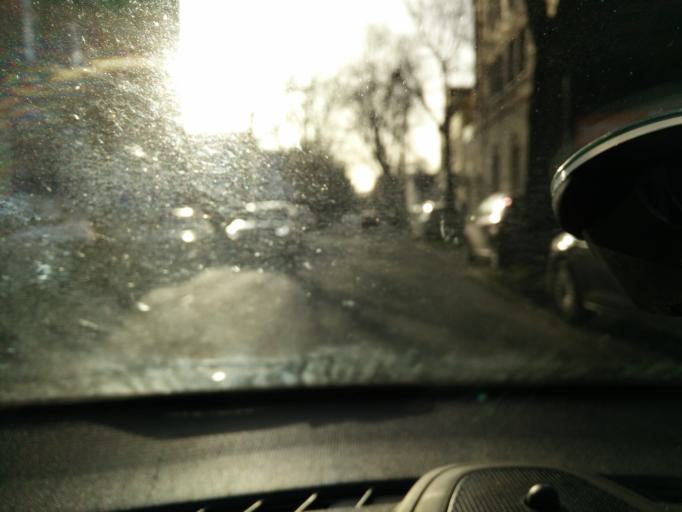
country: DE
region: North Rhine-Westphalia
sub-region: Regierungsbezirk Dusseldorf
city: Essen
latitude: 51.4852
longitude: 7.0192
